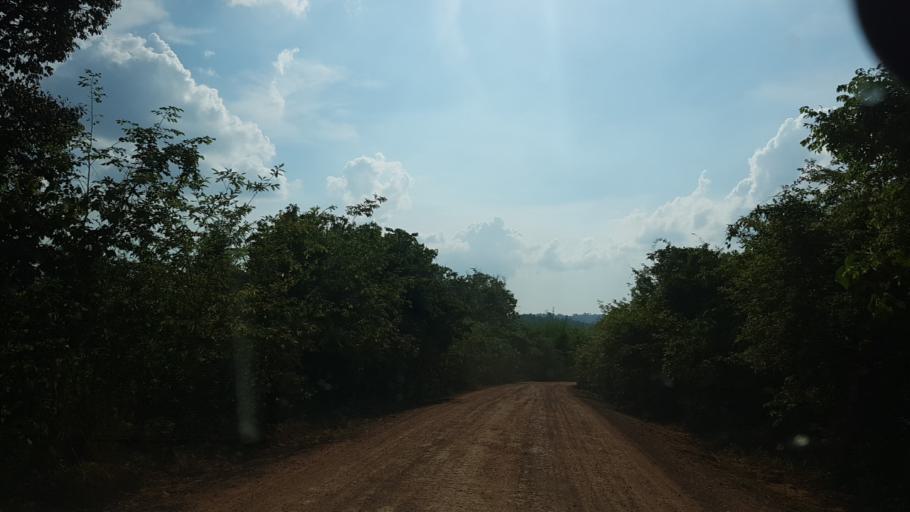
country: LA
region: Vientiane
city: Muang Phon-Hong
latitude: 18.3440
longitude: 102.2925
